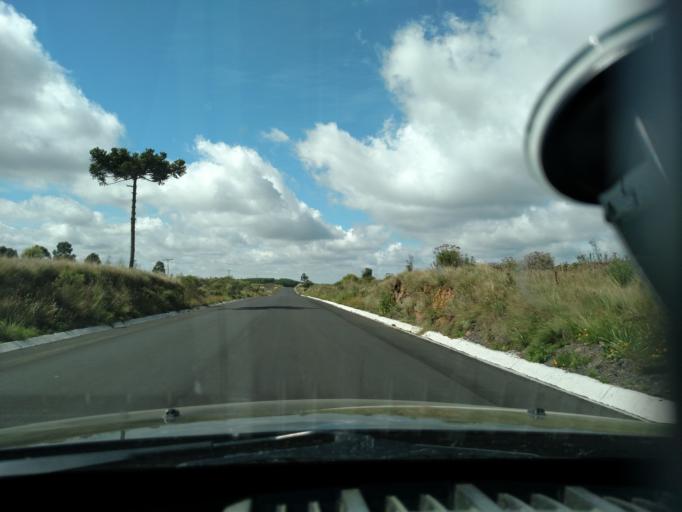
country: BR
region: Santa Catarina
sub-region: Lages
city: Lages
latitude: -27.9915
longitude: -50.0893
